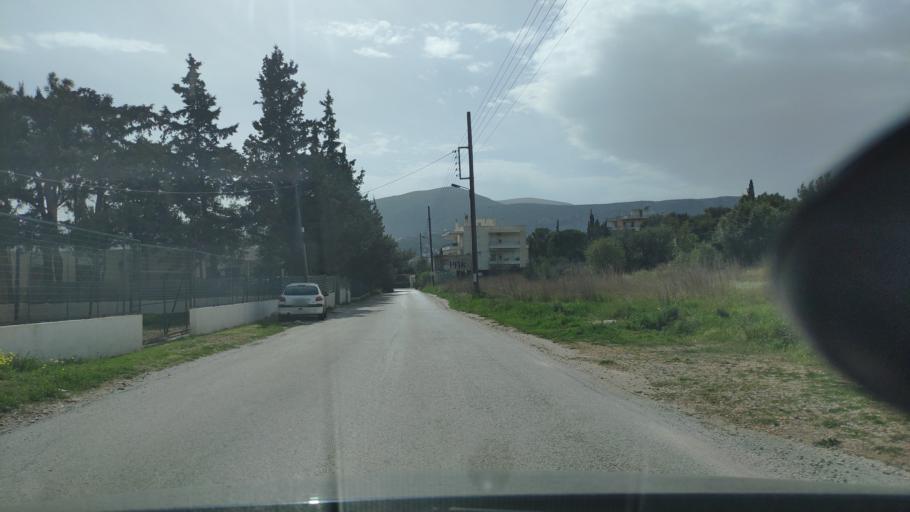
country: GR
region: Attica
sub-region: Nomarchia Anatolikis Attikis
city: Limin Mesoyaias
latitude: 37.8953
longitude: 24.0227
